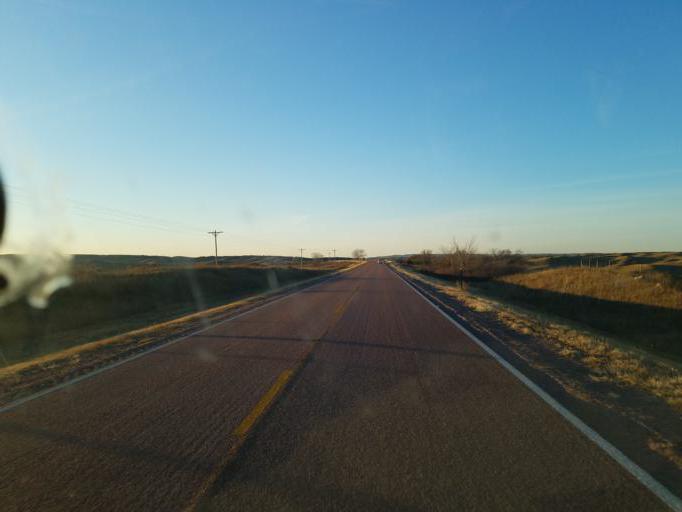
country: US
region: South Dakota
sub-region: Bon Homme County
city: Springfield
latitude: 42.7394
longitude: -97.9113
